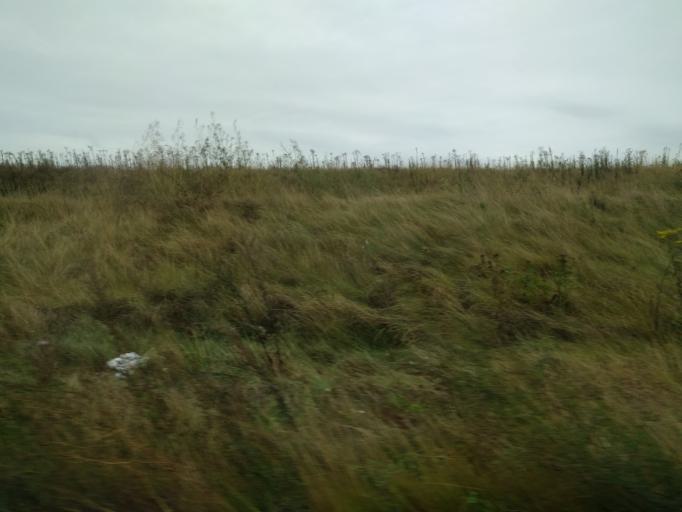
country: DK
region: Zealand
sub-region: Naestved Kommune
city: Fensmark
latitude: 55.2607
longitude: 11.7941
